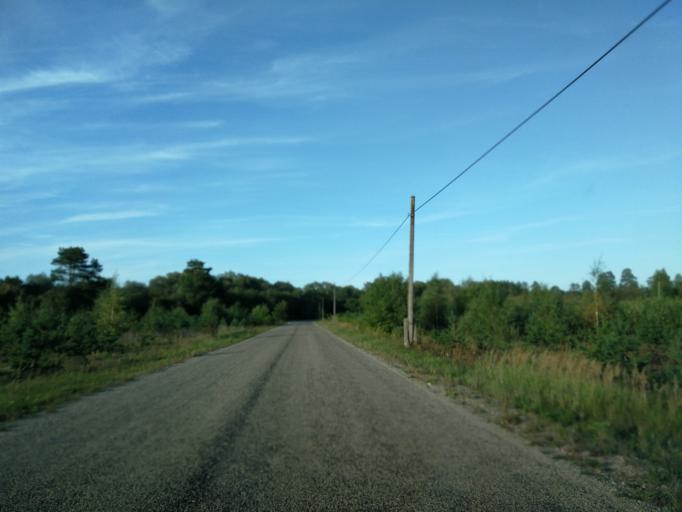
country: LV
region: Garkalne
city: Garkalne
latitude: 57.0801
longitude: 24.4624
